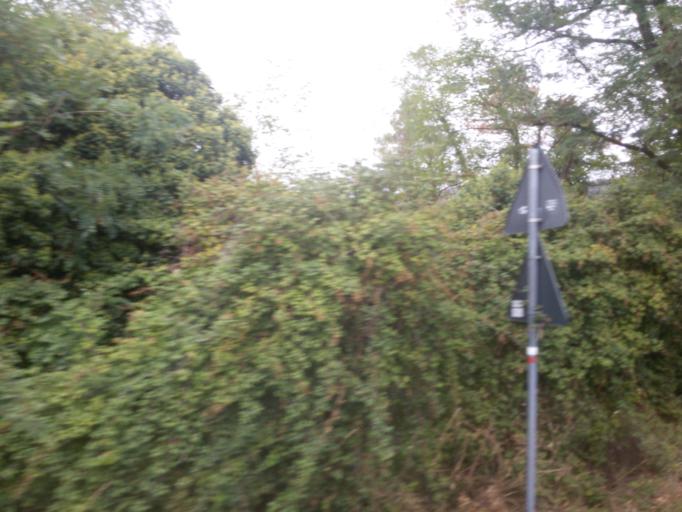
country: IT
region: Liguria
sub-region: Provincia di La Spezia
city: Santo Stefano di Magra
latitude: 44.1607
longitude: 9.9362
